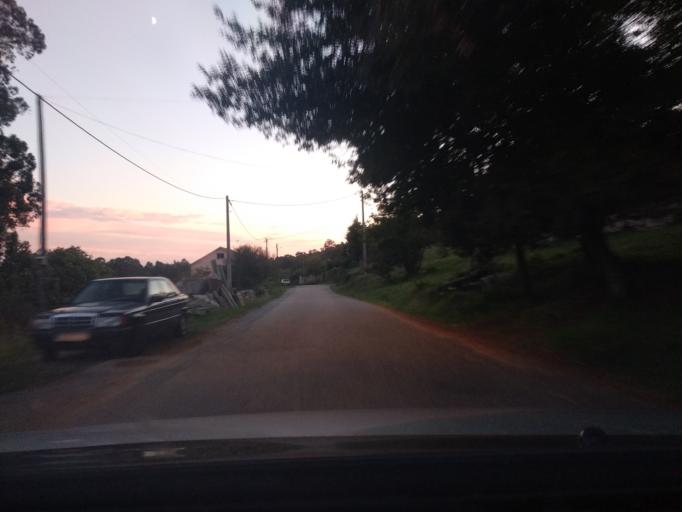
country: ES
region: Galicia
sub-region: Provincia de Pontevedra
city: Moana
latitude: 42.3043
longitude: -8.6993
